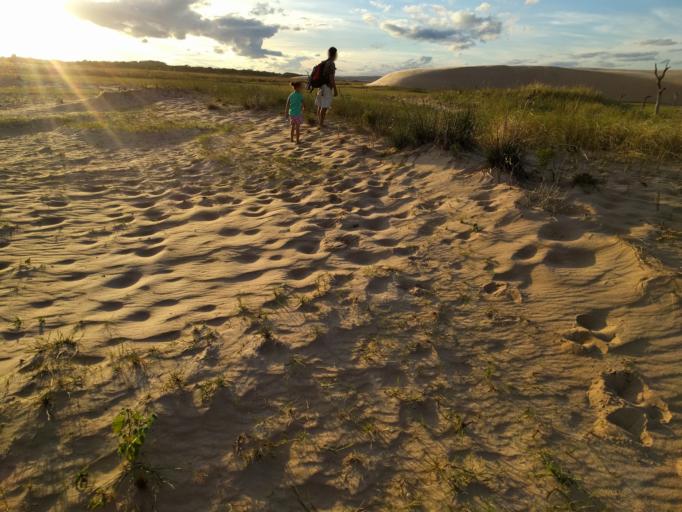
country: BO
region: Santa Cruz
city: Cotoca
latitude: -17.9692
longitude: -63.1471
